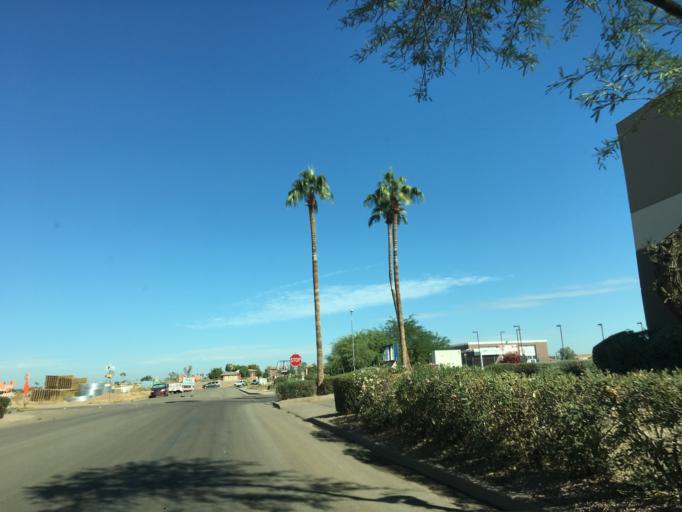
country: US
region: Arizona
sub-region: Maricopa County
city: Tolleson
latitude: 33.4602
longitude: -112.1821
